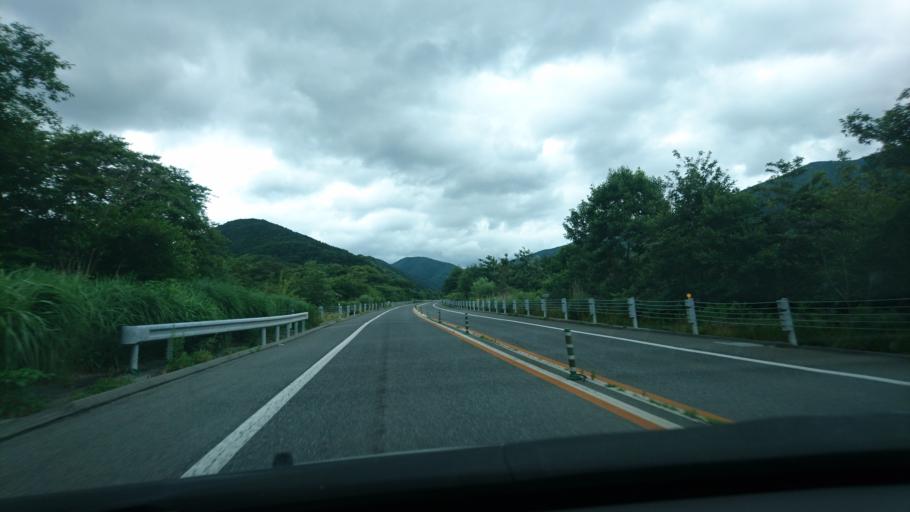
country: JP
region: Iwate
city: Ofunato
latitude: 39.1251
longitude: 141.7288
